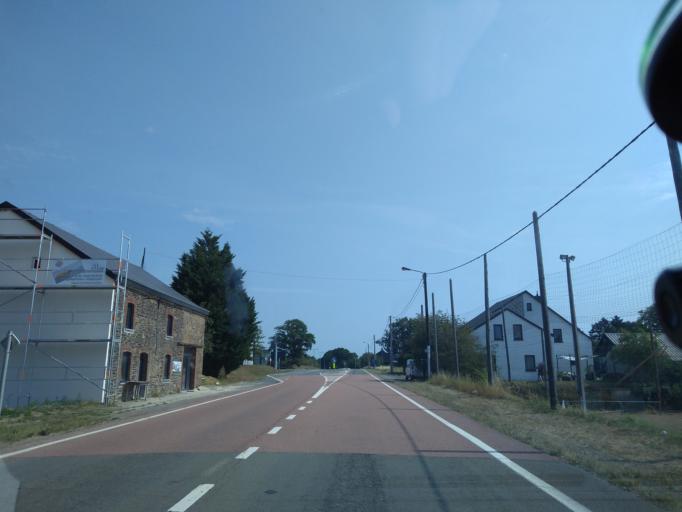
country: BE
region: Wallonia
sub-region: Province du Luxembourg
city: Tenneville
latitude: 50.1460
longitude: 5.5088
